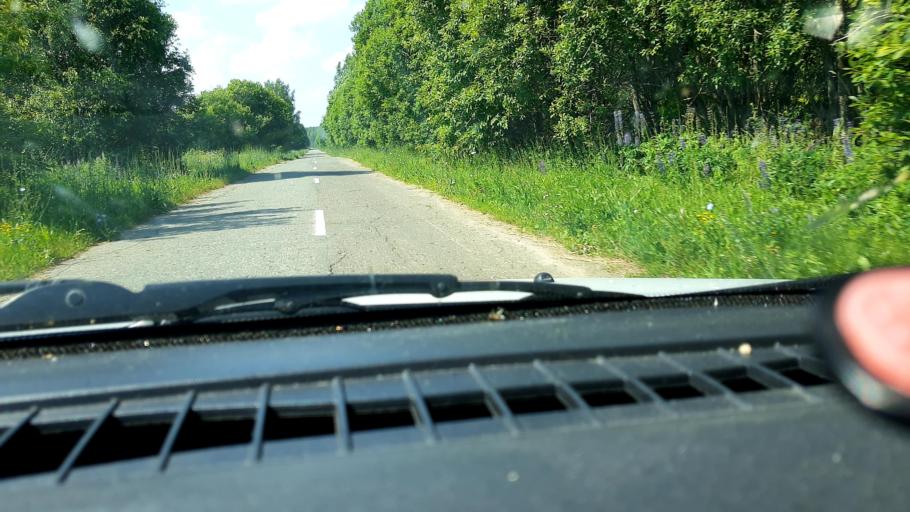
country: RU
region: Nizjnij Novgorod
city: Sharanga
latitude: 57.0584
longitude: 46.5954
